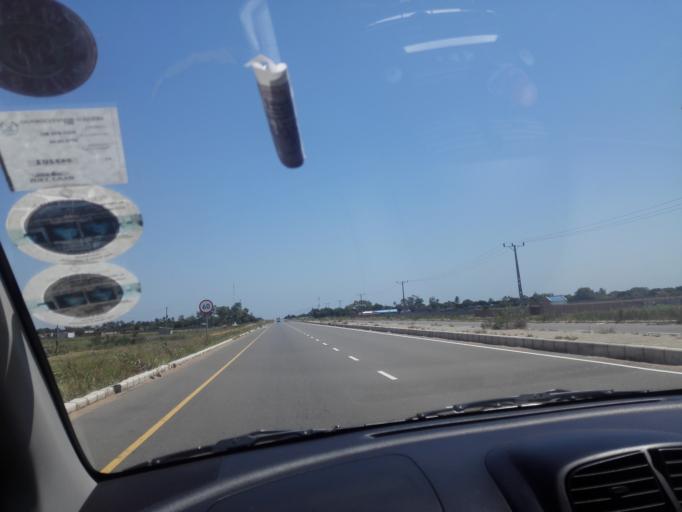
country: MZ
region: Maputo City
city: Maputo
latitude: -25.8231
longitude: 32.6723
